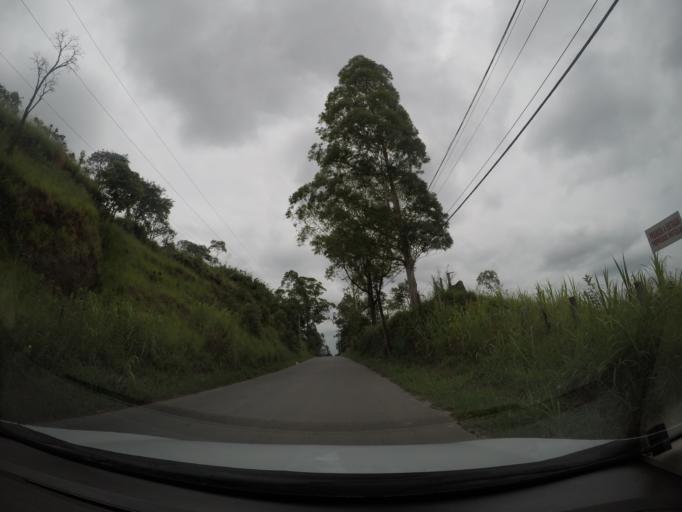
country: BR
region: Sao Paulo
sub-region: Aruja
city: Aruja
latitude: -23.3719
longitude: -46.2976
